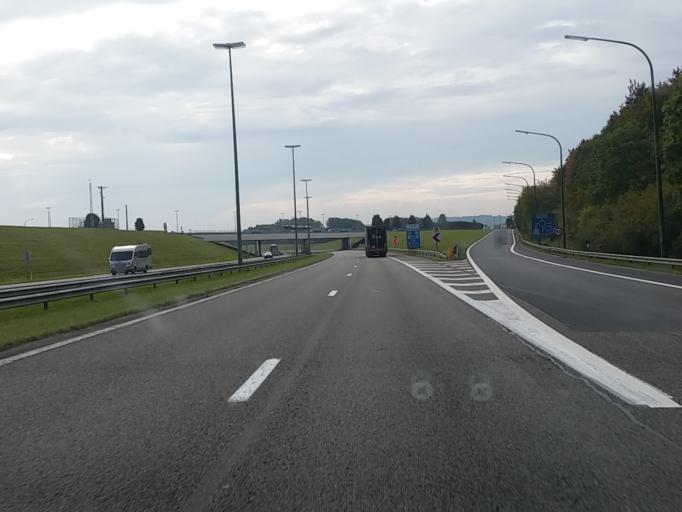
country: BE
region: Wallonia
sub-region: Province du Luxembourg
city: Arlon
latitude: 49.6537
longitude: 5.8173
